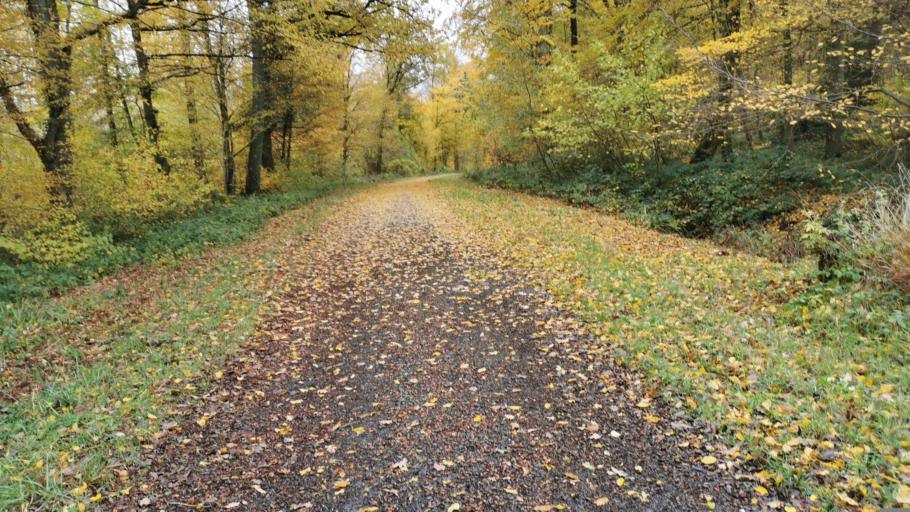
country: FR
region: Picardie
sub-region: Departement de l'Aisne
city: Saint-Gobain
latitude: 49.5862
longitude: 3.3634
